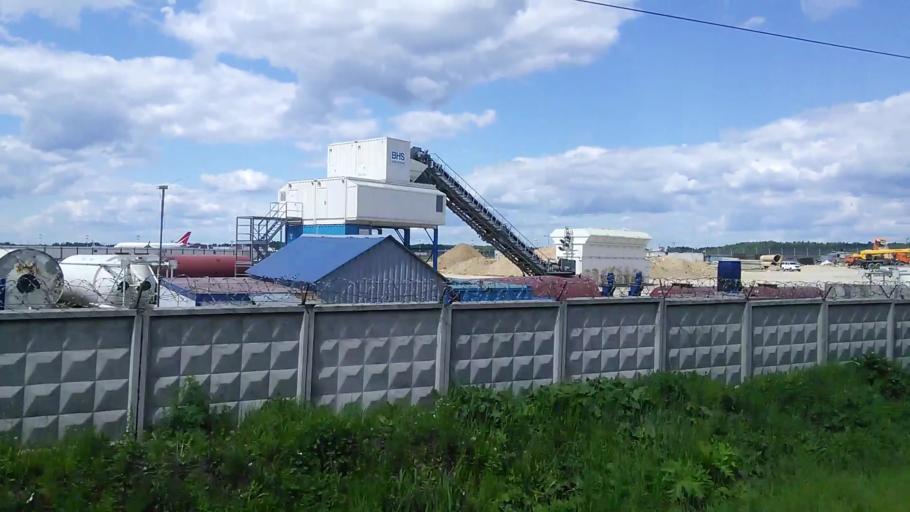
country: RU
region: Moskovskaya
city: Sheremet'yevskiy
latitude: 55.9718
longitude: 37.4467
